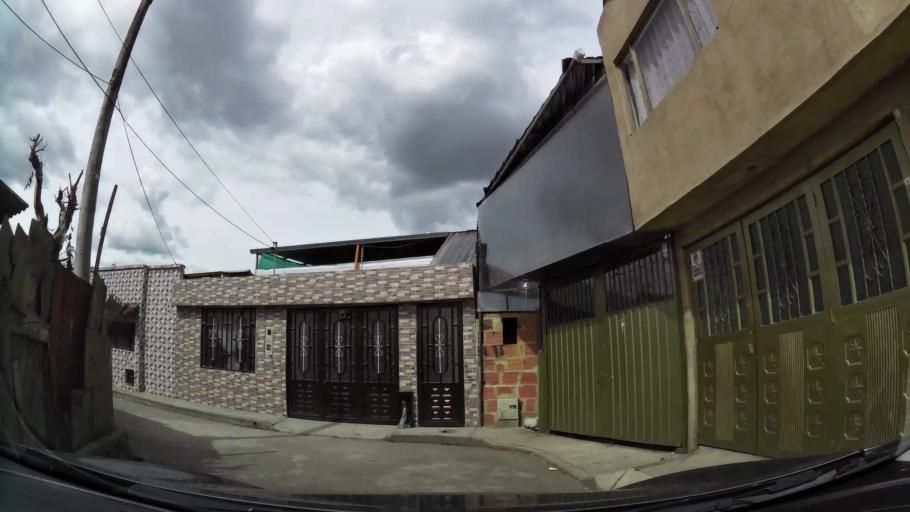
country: CO
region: Cundinamarca
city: Funza
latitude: 4.7078
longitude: -74.1964
